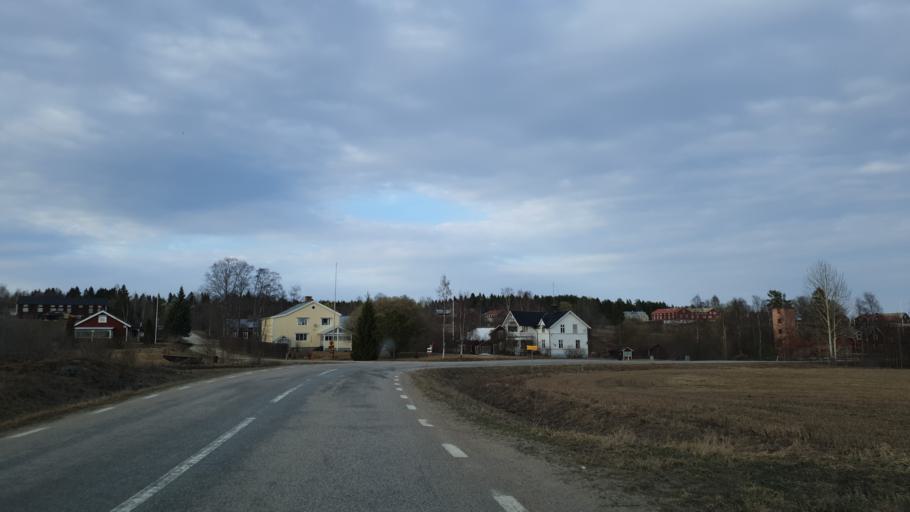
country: SE
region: Gaevleborg
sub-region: Nordanstigs Kommun
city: Bergsjoe
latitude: 61.9782
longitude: 17.2632
